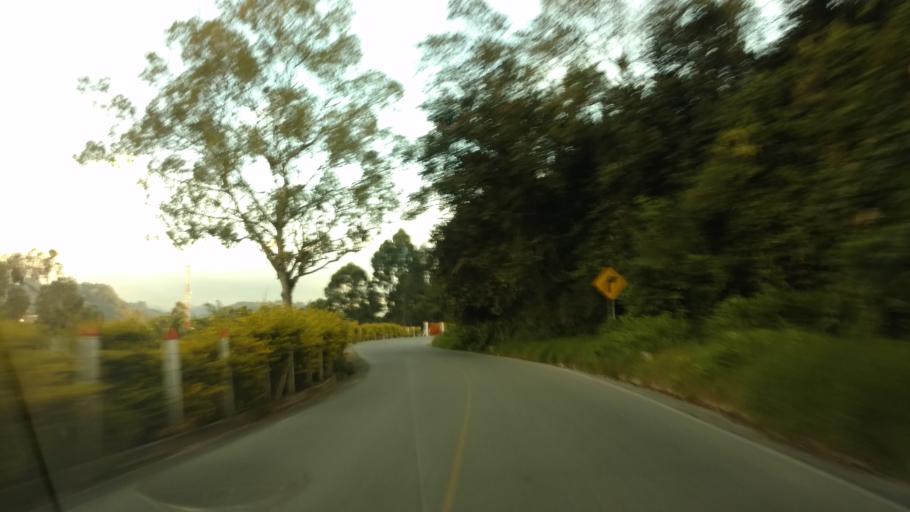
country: CO
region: Caldas
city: Aranzazu
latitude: 5.2870
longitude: -75.4877
